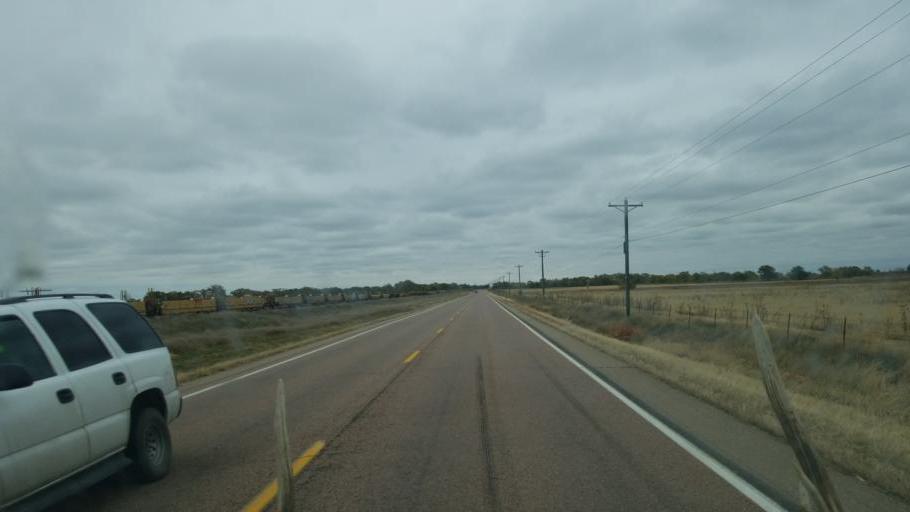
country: US
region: Colorado
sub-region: Crowley County
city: Ordway
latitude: 38.1874
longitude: -103.8724
